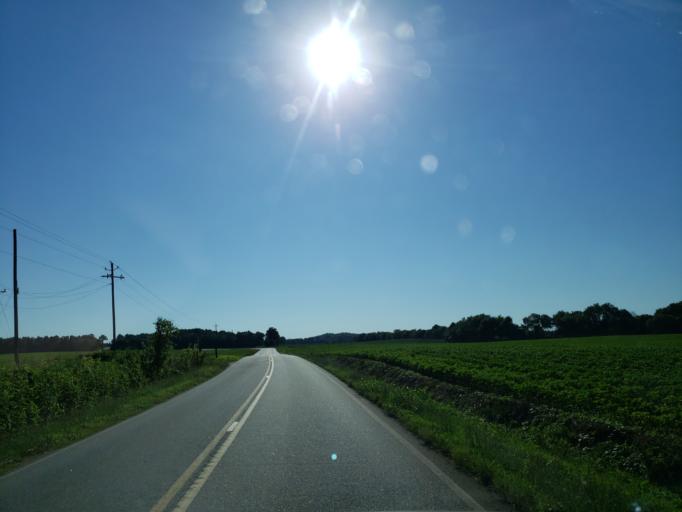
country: US
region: Georgia
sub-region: Bartow County
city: Euharlee
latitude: 34.1085
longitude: -84.9510
